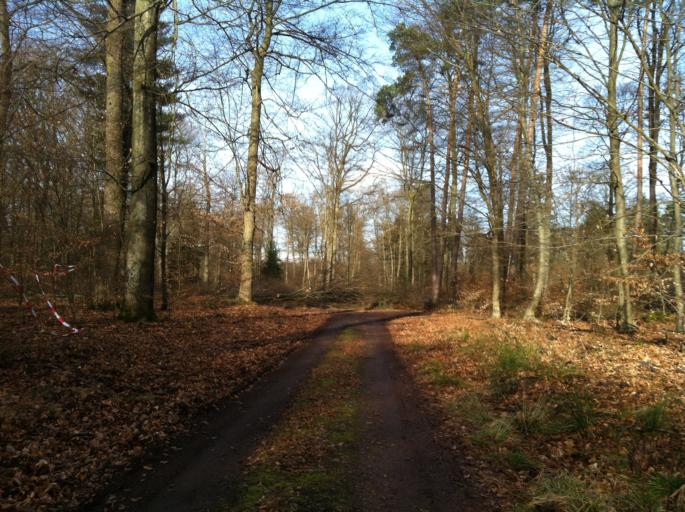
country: DE
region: Hesse
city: Langen
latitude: 50.0138
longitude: 8.6431
